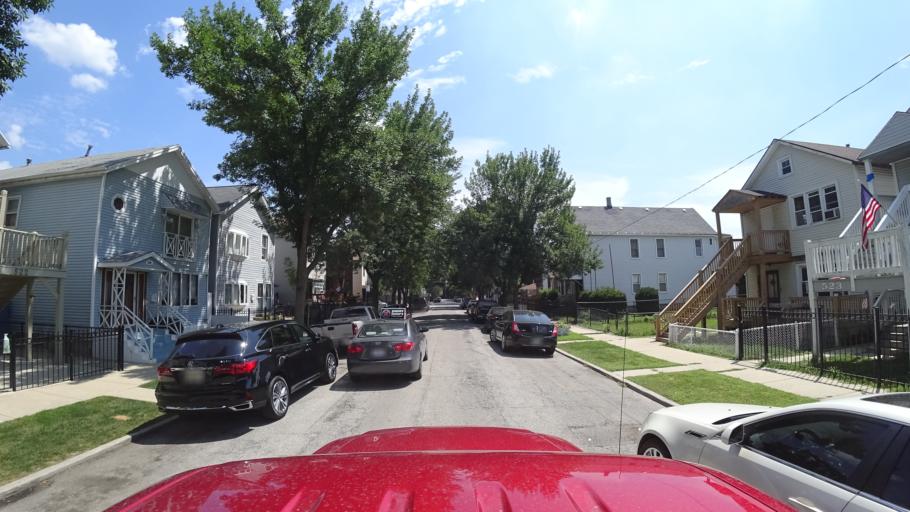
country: US
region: Illinois
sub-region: Cook County
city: Chicago
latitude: 41.8172
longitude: -87.6395
